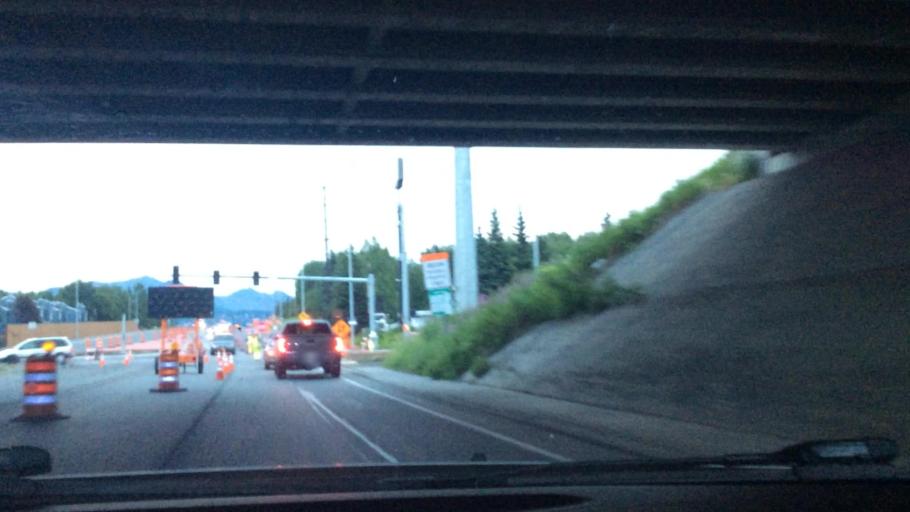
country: US
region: Alaska
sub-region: Anchorage Municipality
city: Anchorage
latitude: 61.1230
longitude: -149.8565
